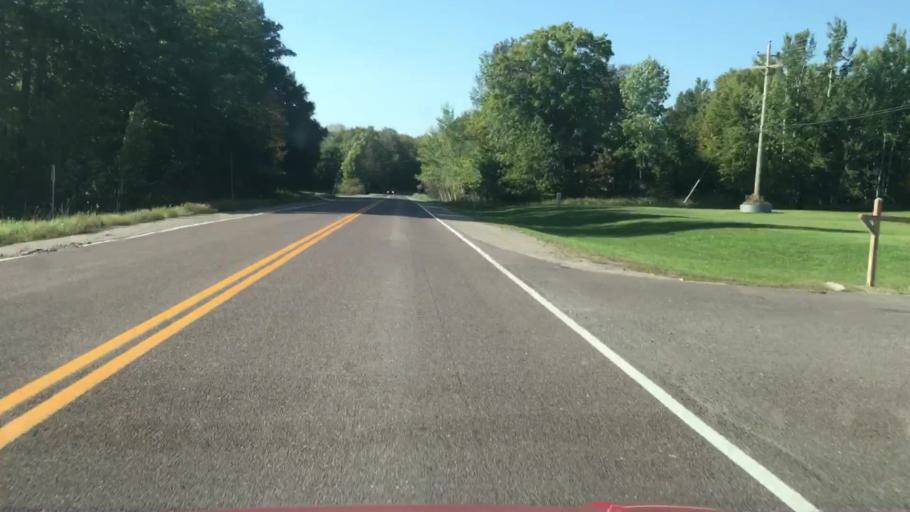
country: US
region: Michigan
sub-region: Chippewa County
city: Sault Ste. Marie
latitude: 46.2785
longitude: -84.0300
